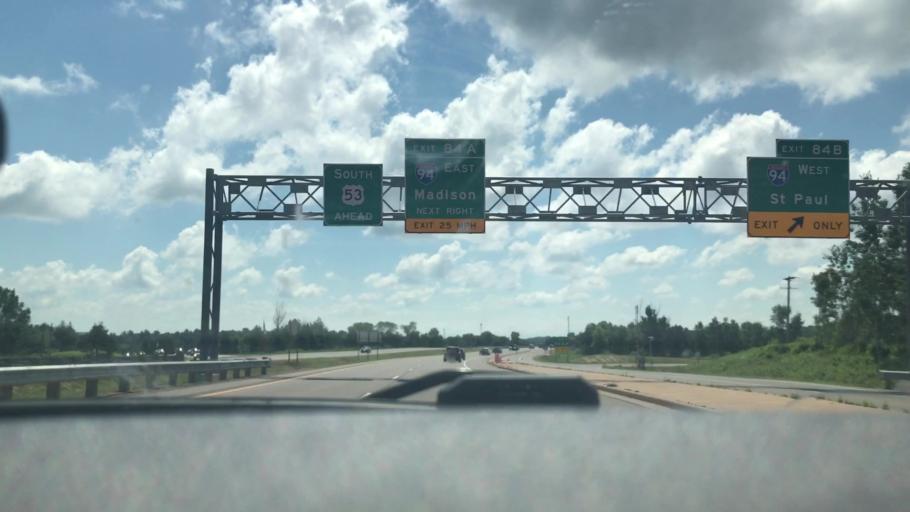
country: US
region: Wisconsin
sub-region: Eau Claire County
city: Altoona
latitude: 44.7704
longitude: -91.4256
